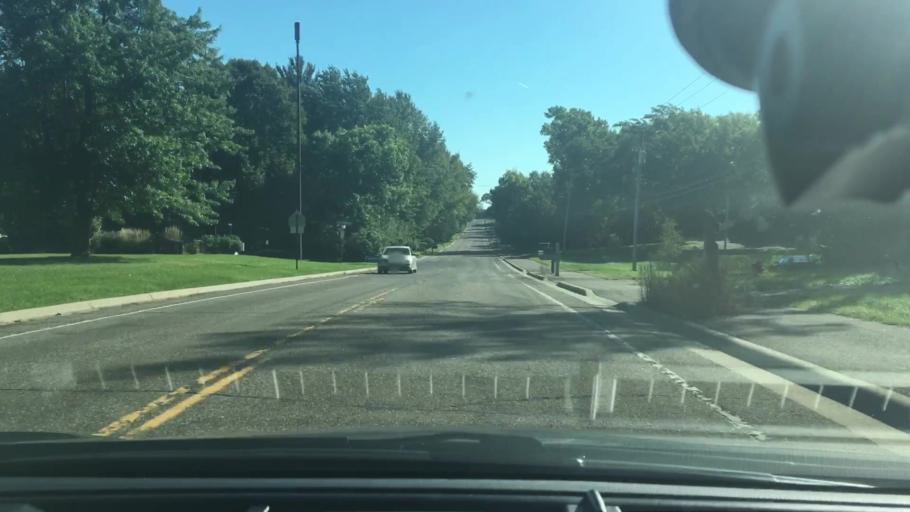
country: US
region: Minnesota
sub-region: Hennepin County
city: Minnetonka Mills
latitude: 44.9788
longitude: -93.4301
